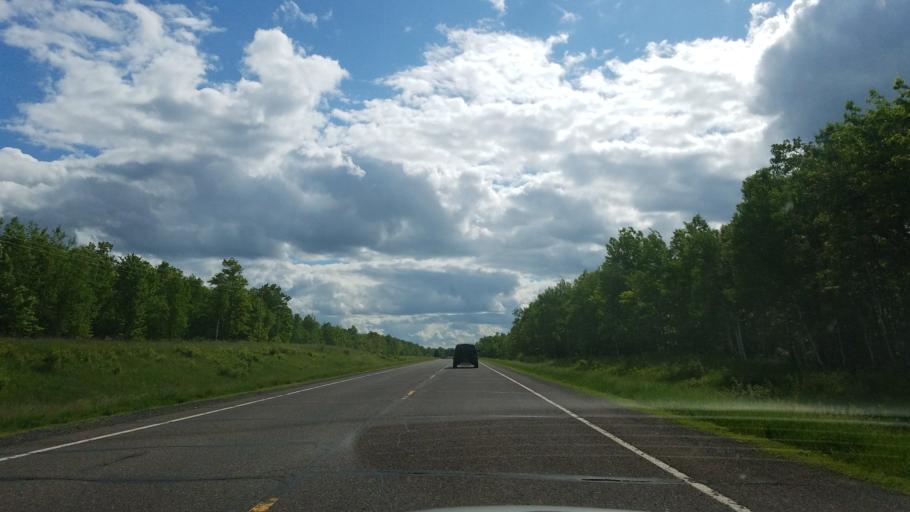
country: US
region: Wisconsin
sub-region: Burnett County
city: Siren
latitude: 46.1829
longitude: -92.1964
